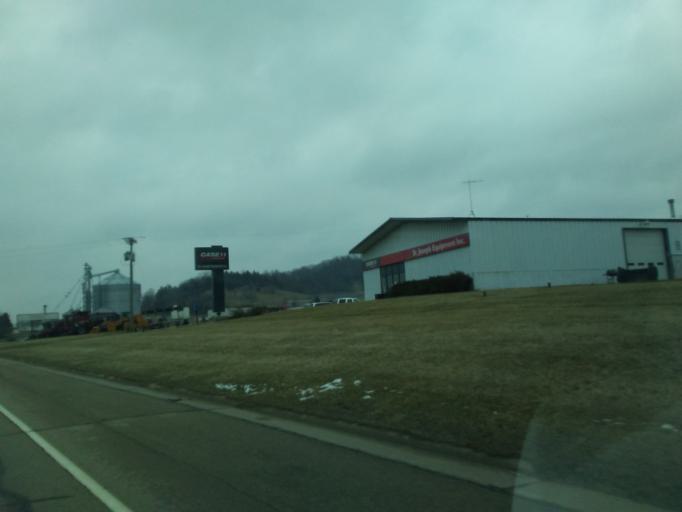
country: US
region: Wisconsin
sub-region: Richland County
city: Richland Center
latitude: 43.2642
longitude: -90.2928
